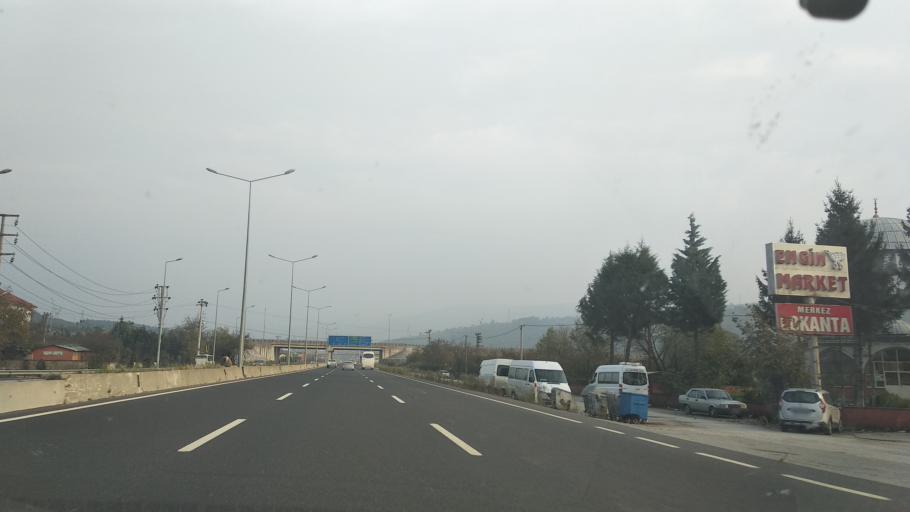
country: TR
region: Duzce
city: Kaynasli
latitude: 40.7965
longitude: 31.2477
